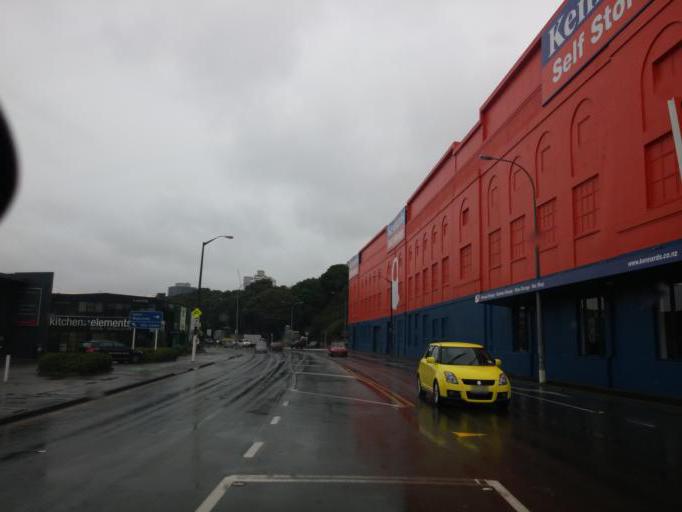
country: NZ
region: Wellington
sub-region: Wellington City
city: Wellington
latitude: -41.2667
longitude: 174.7821
